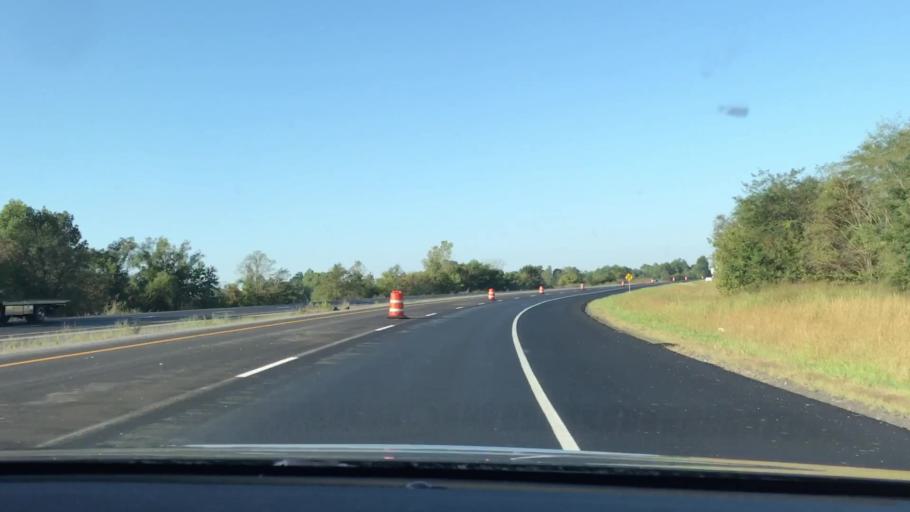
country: US
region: Kentucky
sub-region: Trigg County
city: Cadiz
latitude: 36.8614
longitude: -87.8001
